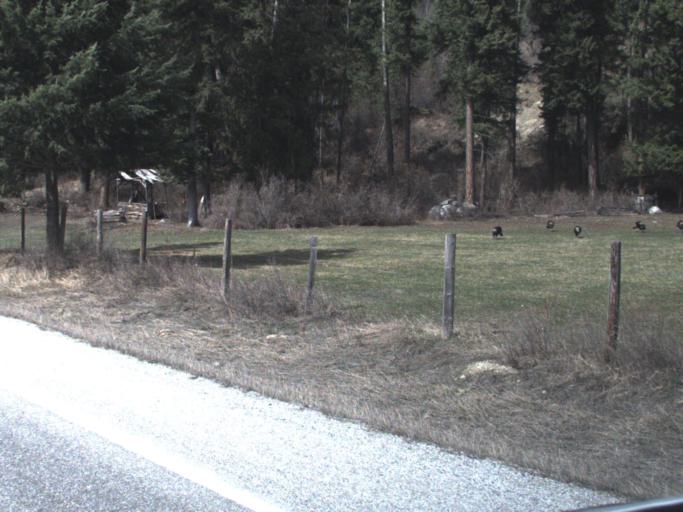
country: US
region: Washington
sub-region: Pend Oreille County
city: Newport
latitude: 48.4749
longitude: -117.2941
